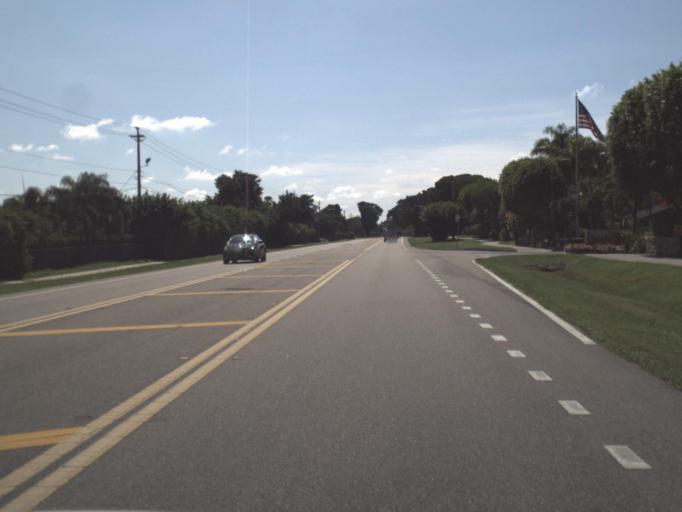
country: US
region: Florida
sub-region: Sarasota County
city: Siesta Key
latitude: 27.3476
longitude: -82.6048
